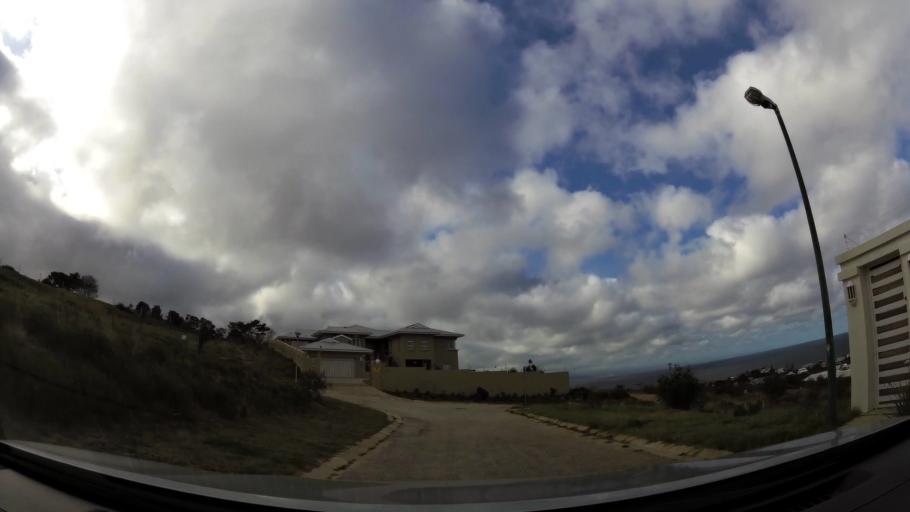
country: ZA
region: Western Cape
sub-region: Eden District Municipality
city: Plettenberg Bay
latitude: -34.0830
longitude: 23.3584
